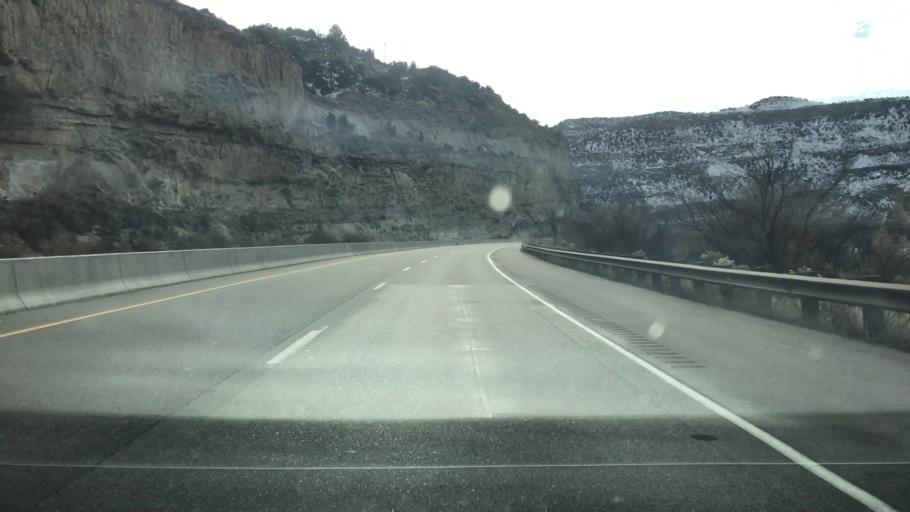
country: US
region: Colorado
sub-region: Mesa County
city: Palisade
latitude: 39.2505
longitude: -108.2573
